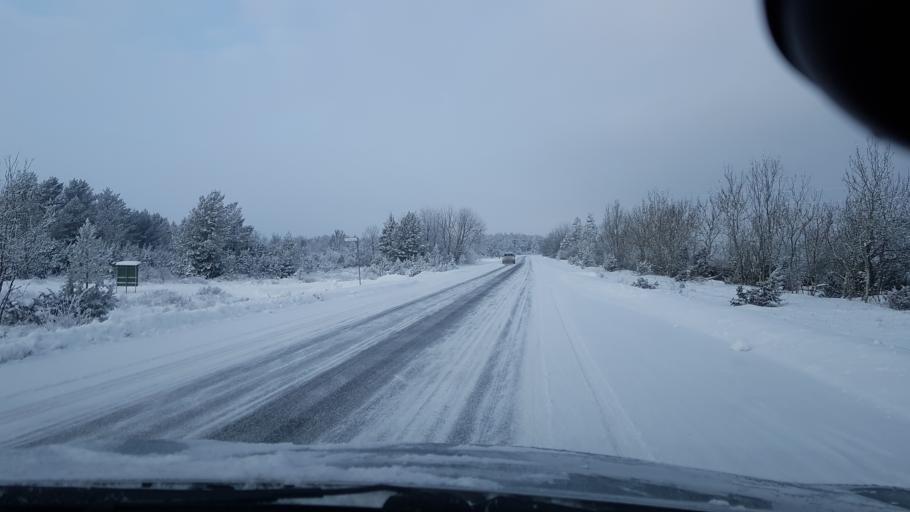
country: EE
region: Harju
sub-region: Keila linn
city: Keila
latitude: 59.3467
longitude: 24.4319
